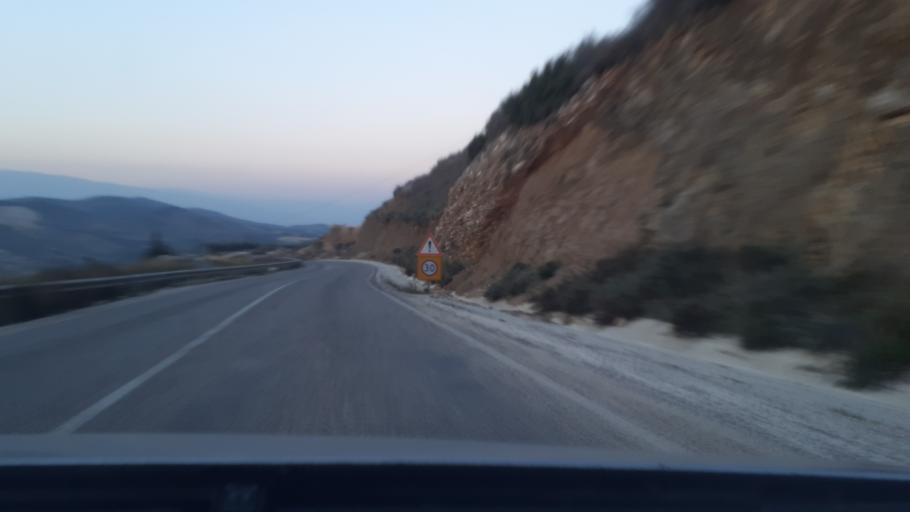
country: TR
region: Hatay
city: Dursunlu
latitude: 36.1707
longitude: 36.1864
